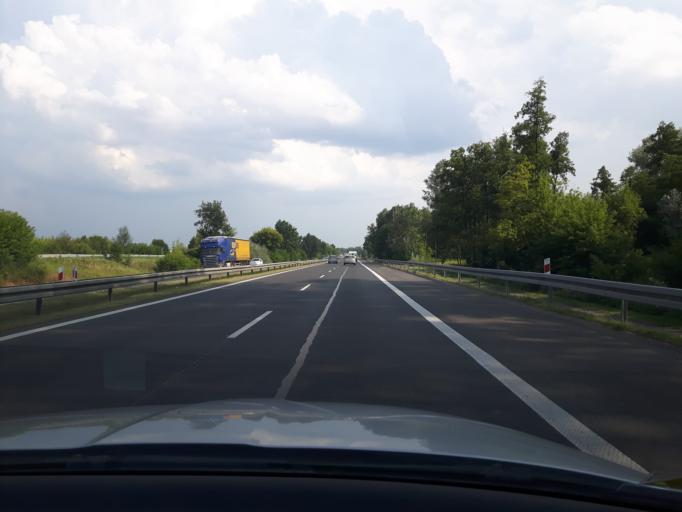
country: PL
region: Masovian Voivodeship
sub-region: Powiat nowodworski
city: Nowy Dwor Mazowiecki
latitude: 52.4027
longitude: 20.7083
